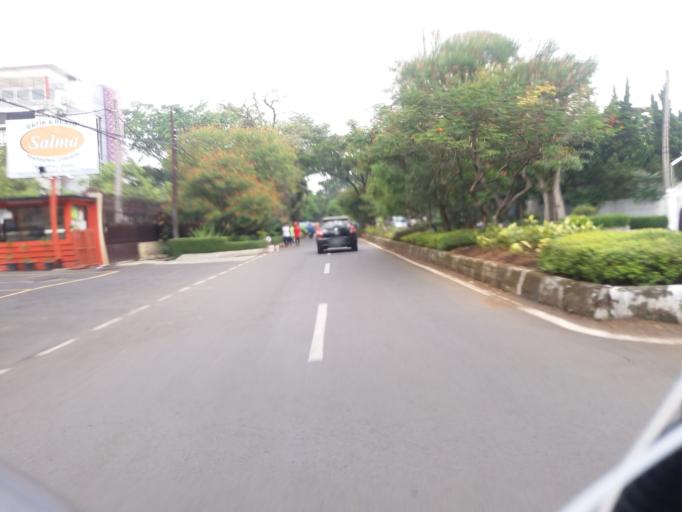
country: ID
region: West Java
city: Bandung
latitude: -6.9027
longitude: 107.6241
